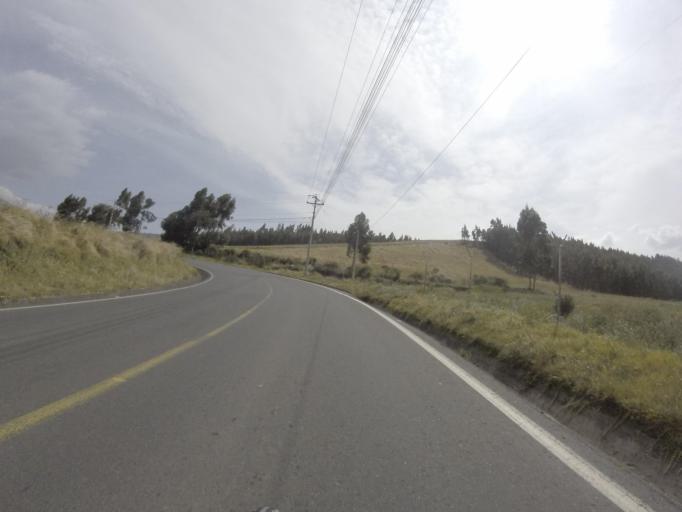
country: EC
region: Pichincha
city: Cayambe
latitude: 0.1223
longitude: -78.0853
